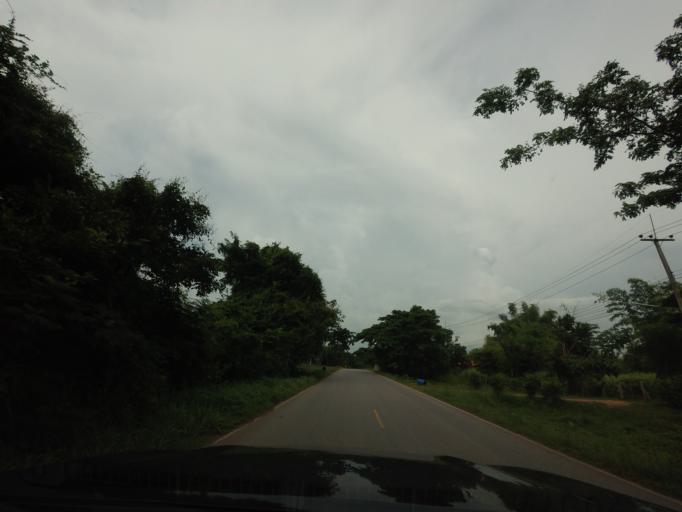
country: TH
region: Changwat Nong Bua Lamphu
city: Suwannakhuha
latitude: 17.4770
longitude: 102.3591
